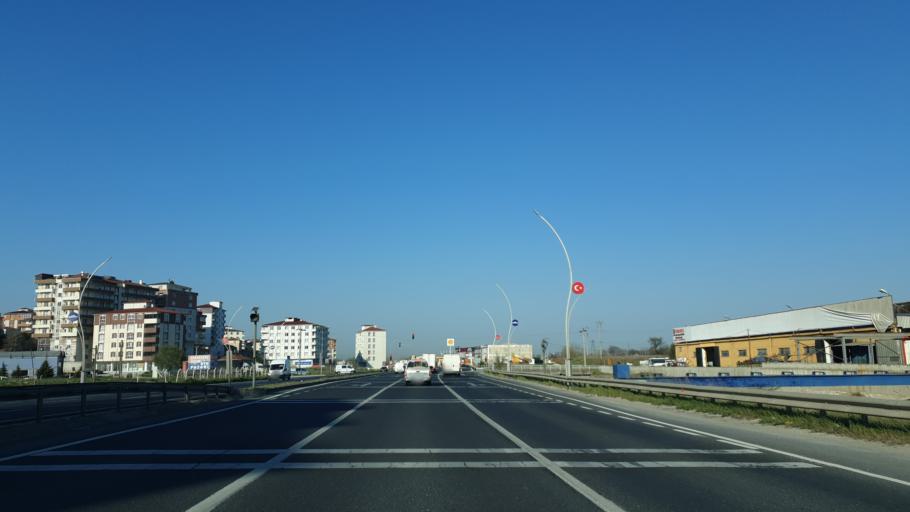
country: TR
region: Tekirdag
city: Cerkezkoey
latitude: 41.2725
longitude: 27.9660
